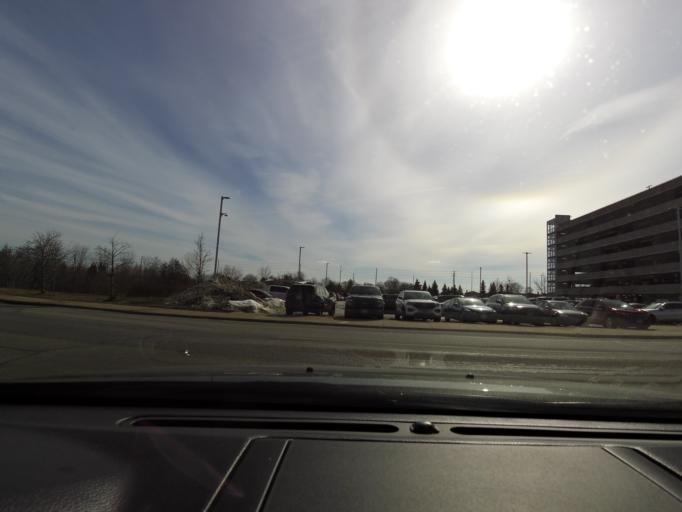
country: CA
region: Ontario
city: Brampton
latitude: 43.7493
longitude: -79.7417
